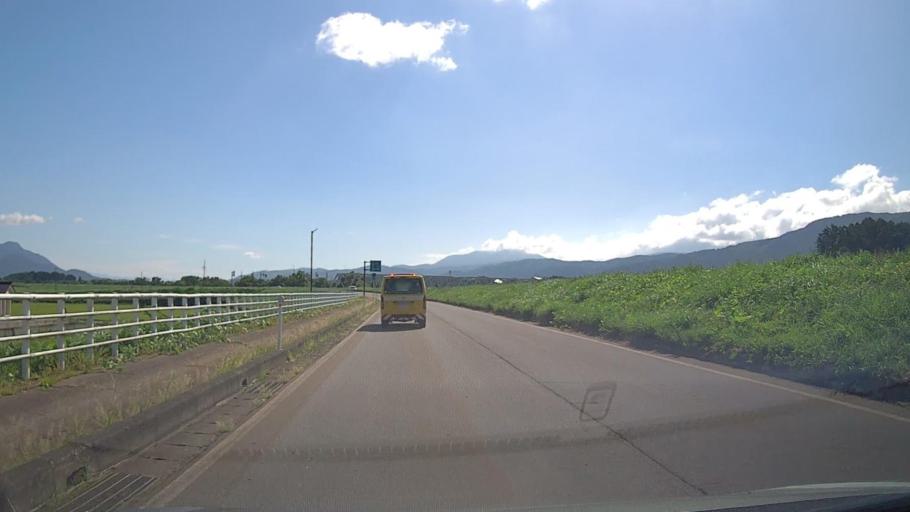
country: JP
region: Nagano
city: Iiyama
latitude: 36.9180
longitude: 138.4012
